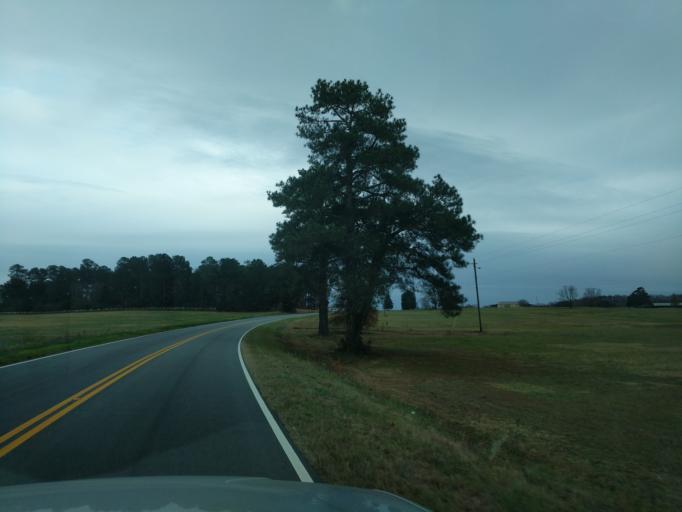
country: US
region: South Carolina
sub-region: Laurens County
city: Laurens
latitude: 34.3729
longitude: -81.9962
